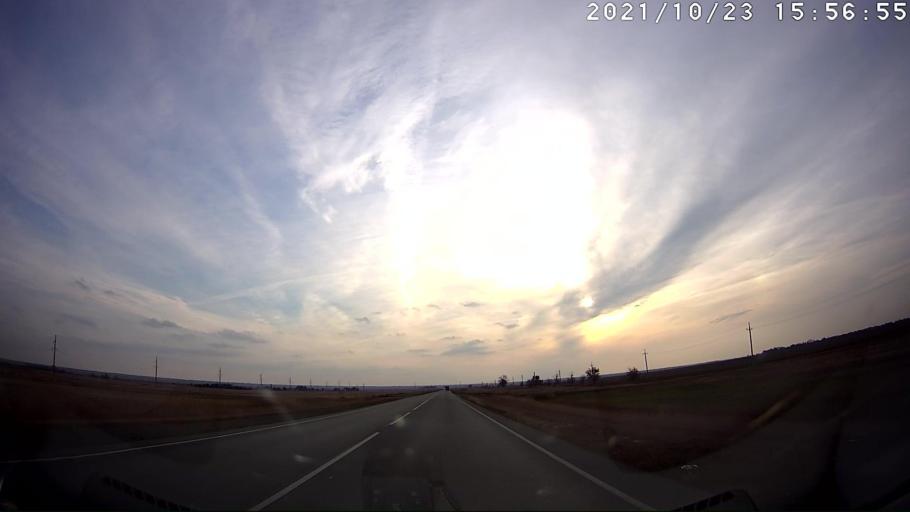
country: RU
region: Kalmykiya
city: Sadovoye
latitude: 47.9527
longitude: 43.9412
